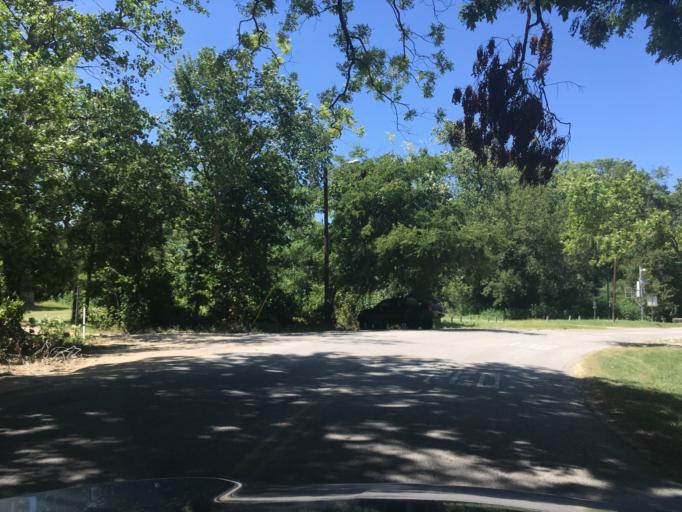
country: US
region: Texas
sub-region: Dallas County
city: Highland Park
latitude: 32.8575
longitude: -96.7323
